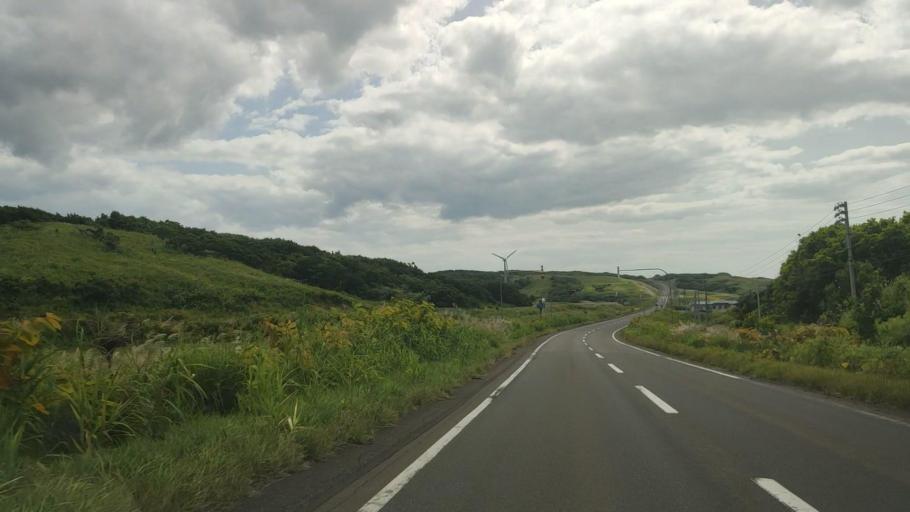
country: JP
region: Hokkaido
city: Rumoi
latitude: 44.5976
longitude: 141.7916
